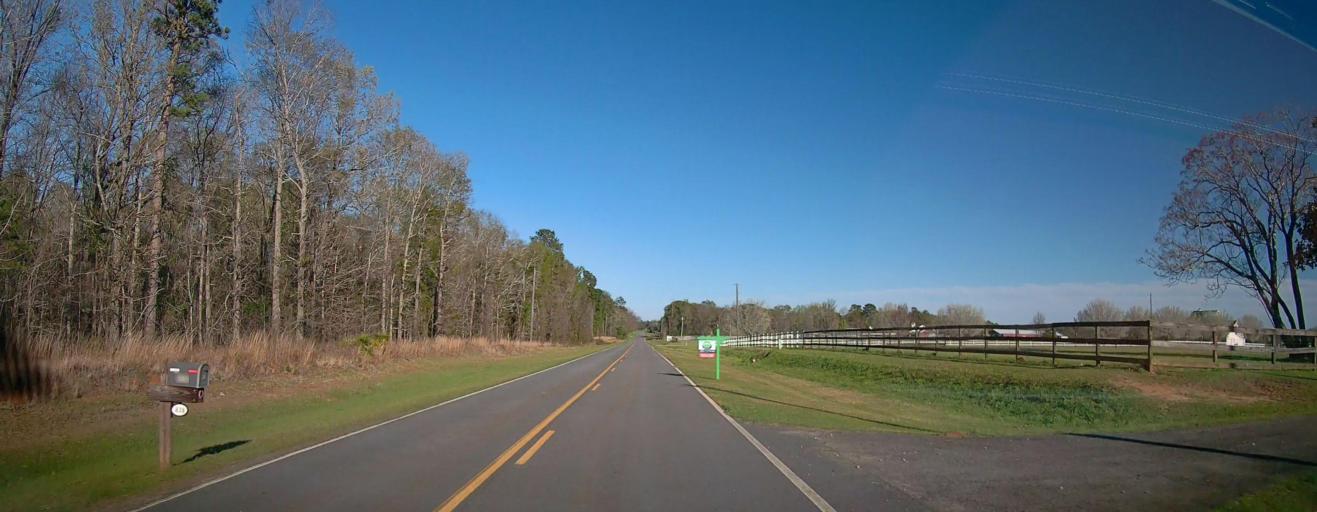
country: US
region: Georgia
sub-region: Pulaski County
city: Hawkinsville
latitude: 32.3475
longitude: -83.5866
